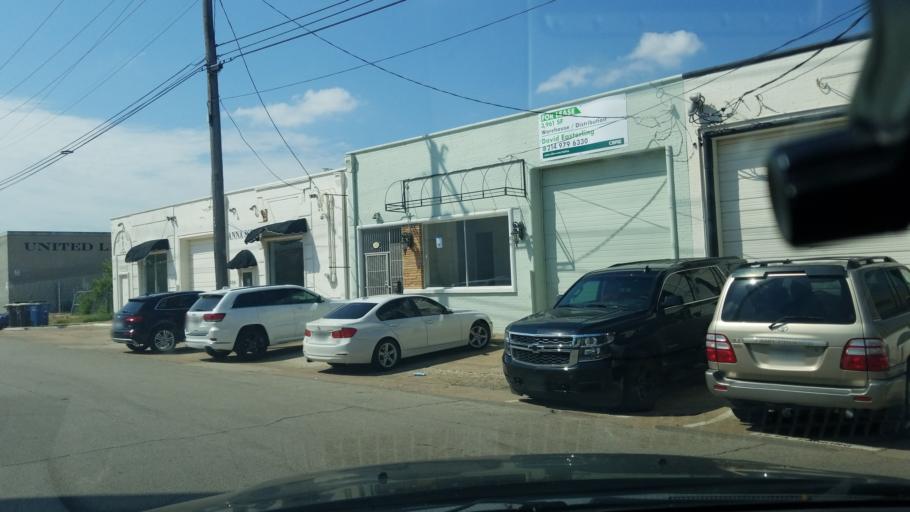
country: US
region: Texas
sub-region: Dallas County
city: Dallas
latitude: 32.7882
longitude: -96.8233
